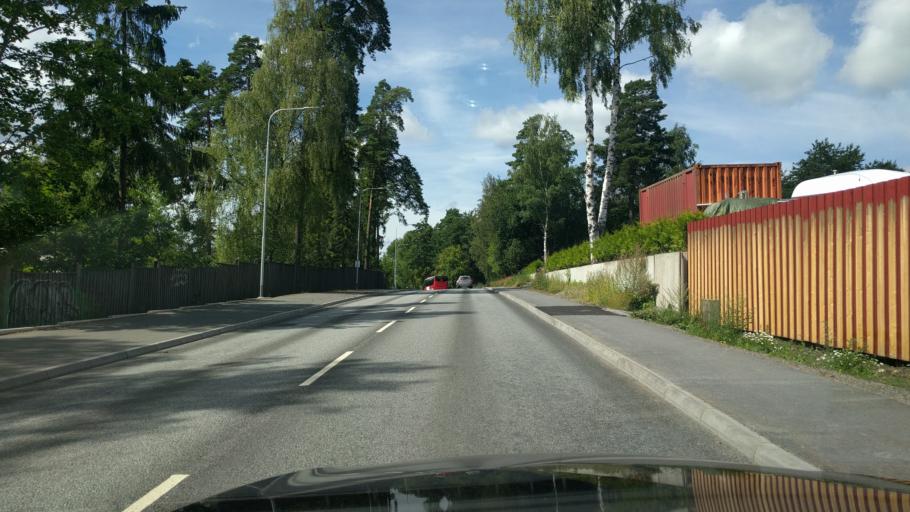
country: SE
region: Stockholm
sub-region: Taby Kommun
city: Taby
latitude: 59.4546
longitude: 18.0402
